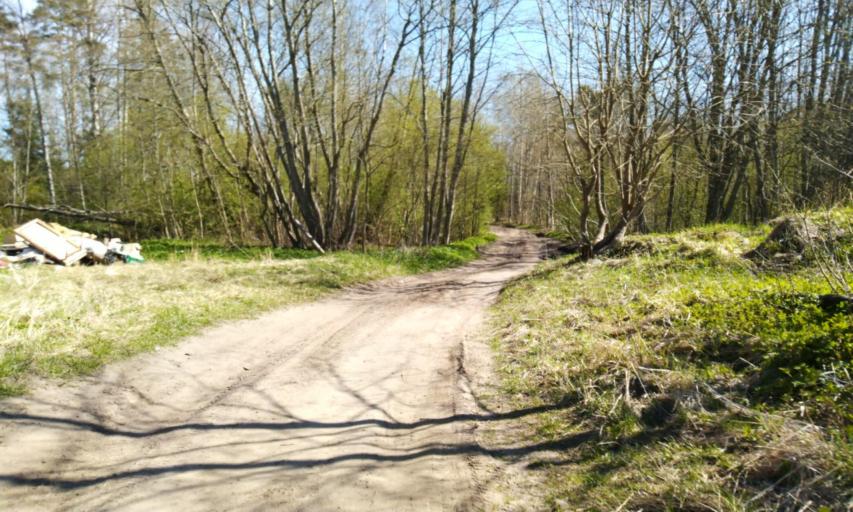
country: RU
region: Leningrad
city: Garbolovo
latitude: 60.4220
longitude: 30.4707
